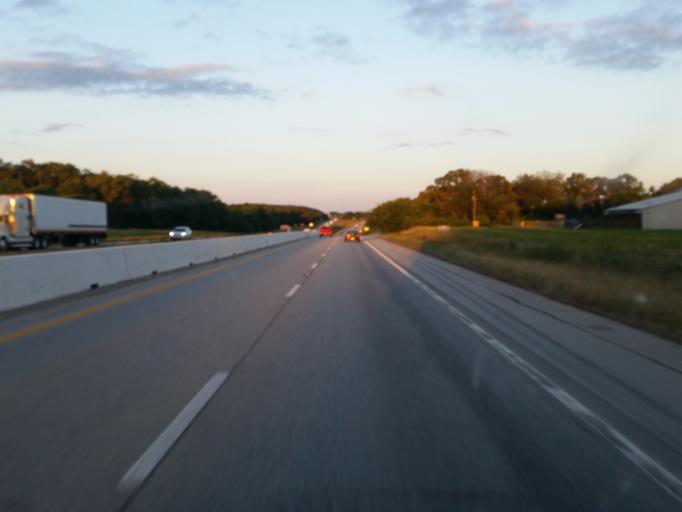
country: US
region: Texas
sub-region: Smith County
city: Hideaway
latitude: 32.4892
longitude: -95.5467
